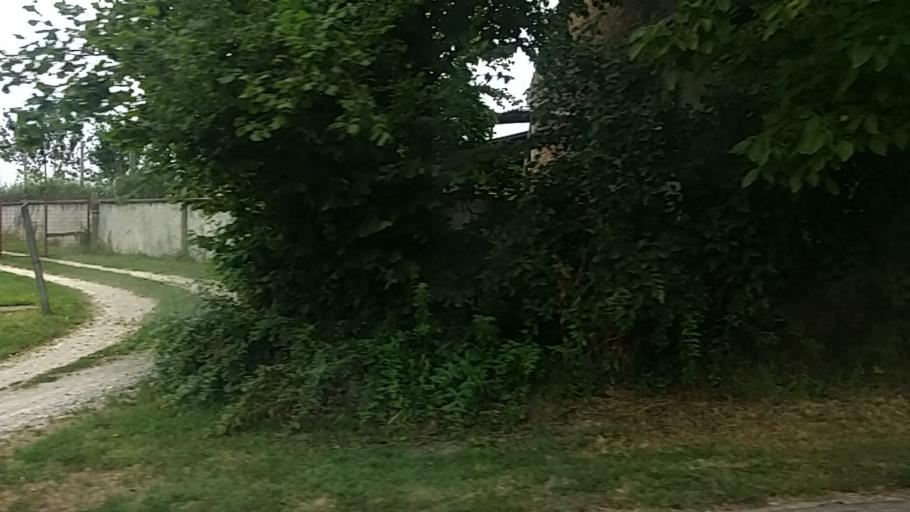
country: HU
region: Baranya
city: Boly
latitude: 45.9747
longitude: 18.5150
